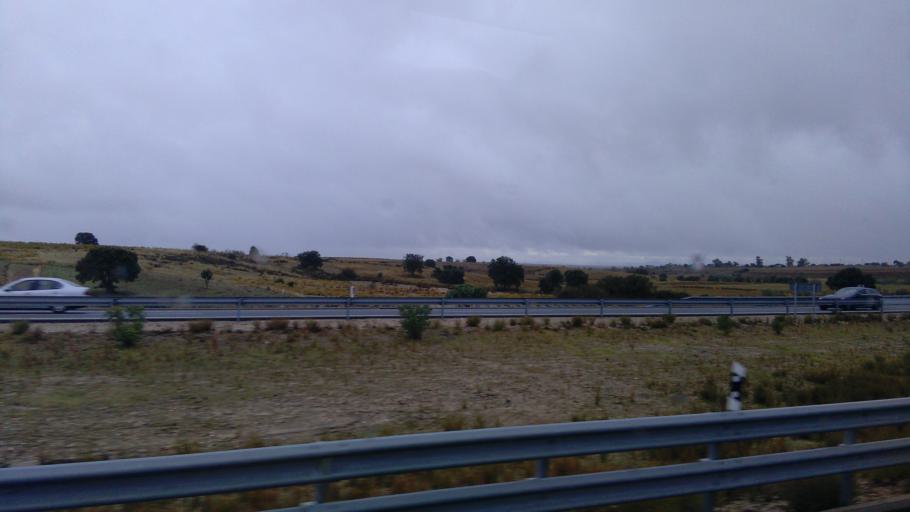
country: ES
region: Castille-La Mancha
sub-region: Province of Toledo
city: La Torre de Esteban Hambran
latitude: 40.1669
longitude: -4.1668
